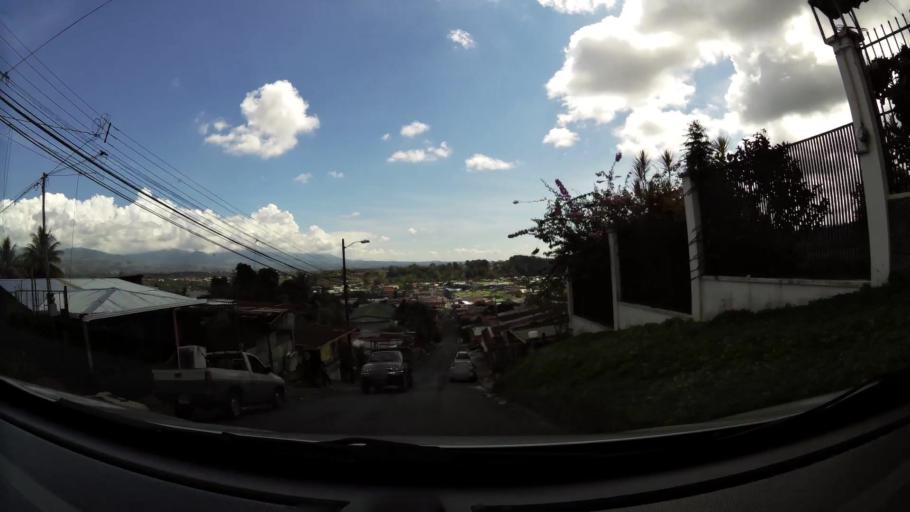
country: CR
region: San Jose
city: San Isidro
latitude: 9.3721
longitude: -83.7096
